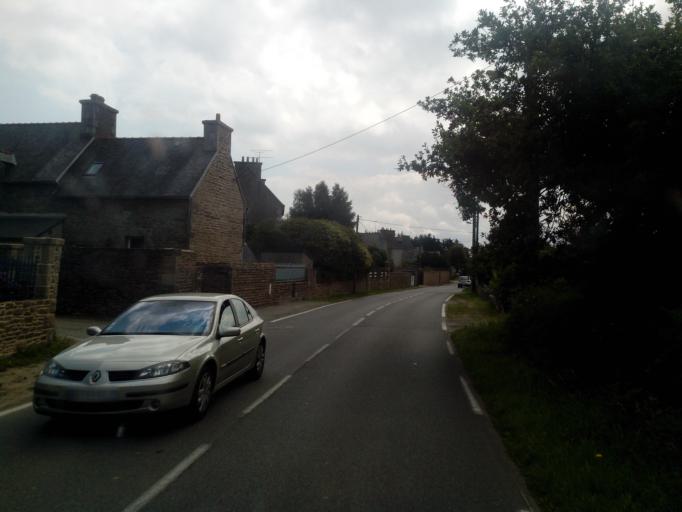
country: FR
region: Brittany
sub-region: Departement des Cotes-d'Armor
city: Plouezec
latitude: 48.7438
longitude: -2.9812
